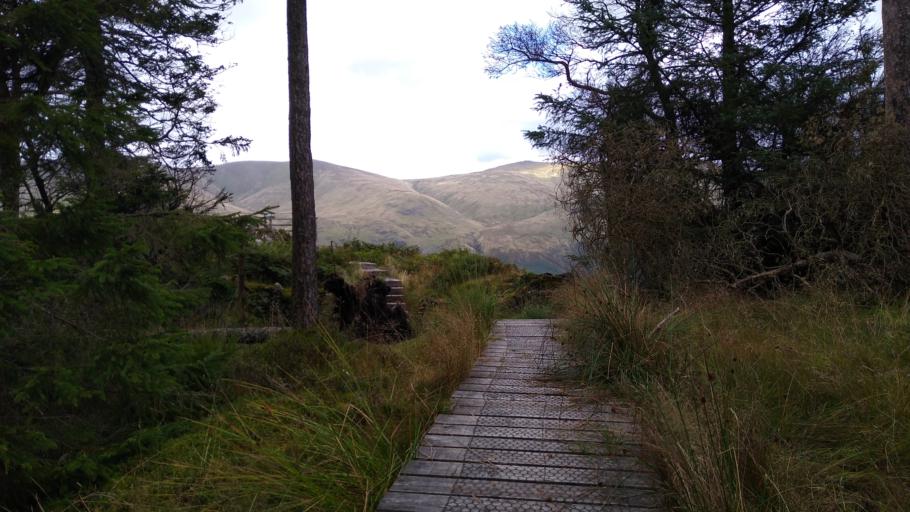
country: GB
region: England
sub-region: Cumbria
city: Keswick
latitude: 54.5592
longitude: -3.0792
